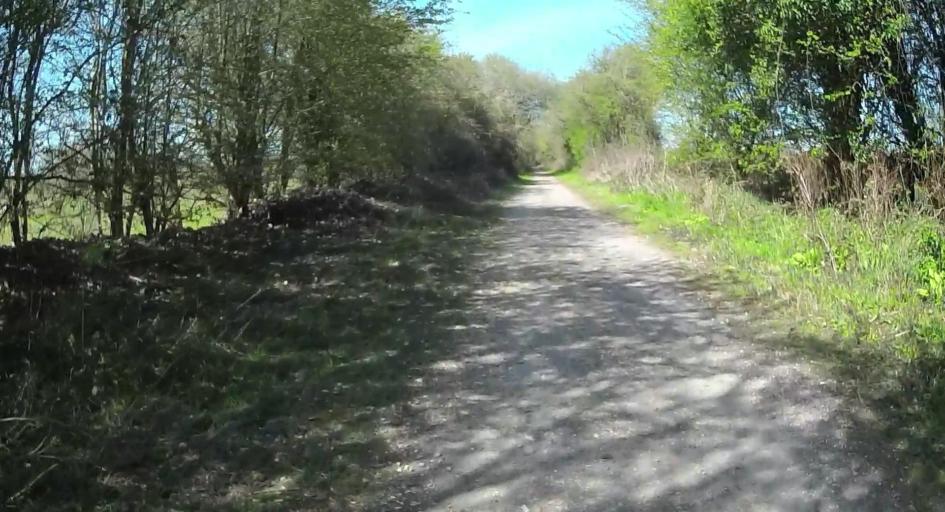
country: GB
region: England
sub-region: Hampshire
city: Romsey
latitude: 51.0639
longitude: -1.5147
